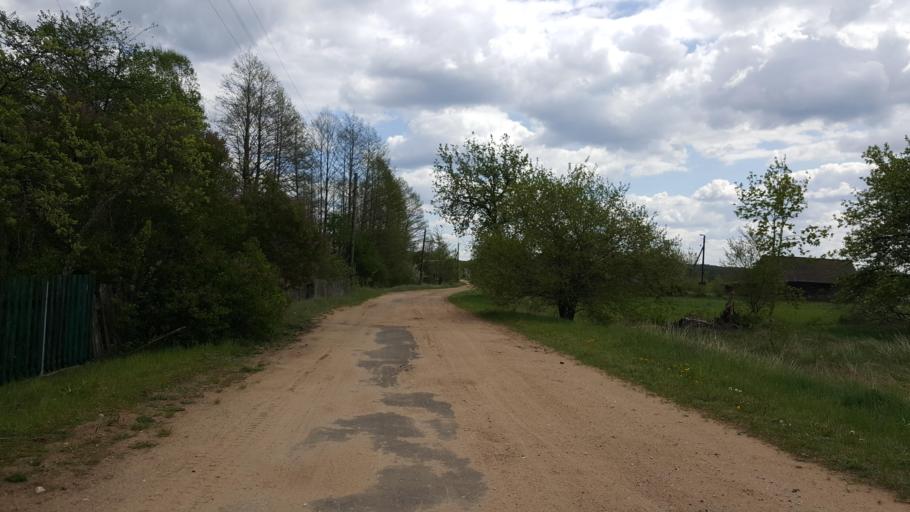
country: BY
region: Brest
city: Zhabinka
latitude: 52.3920
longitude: 24.0168
